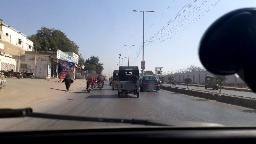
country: PK
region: Sindh
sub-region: Karachi District
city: Karachi
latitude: 24.8970
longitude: 67.0999
